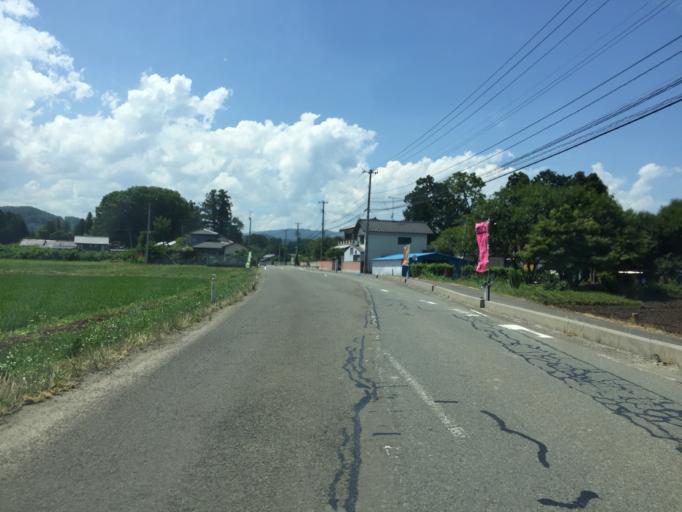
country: JP
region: Fukushima
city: Namie
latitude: 37.7171
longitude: 140.9379
